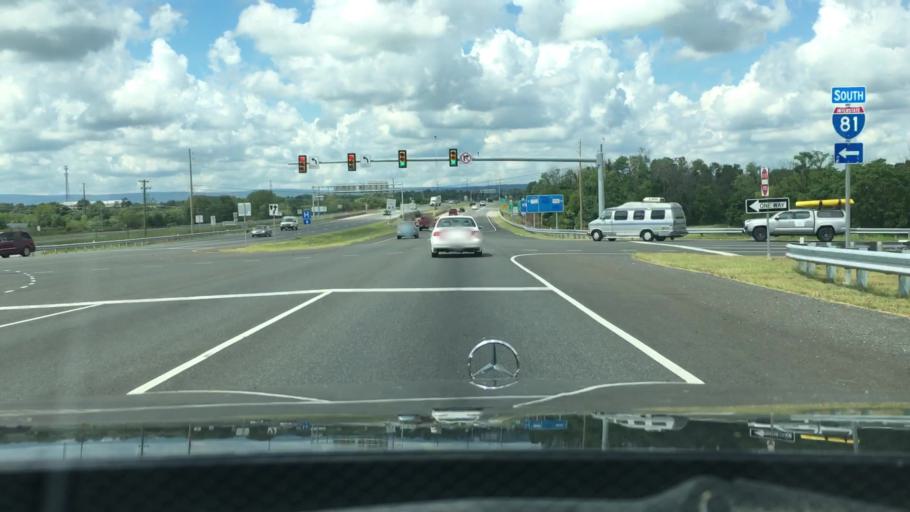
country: US
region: Virginia
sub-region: Frederick County
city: Stephens City
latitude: 39.1213
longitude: -78.1928
